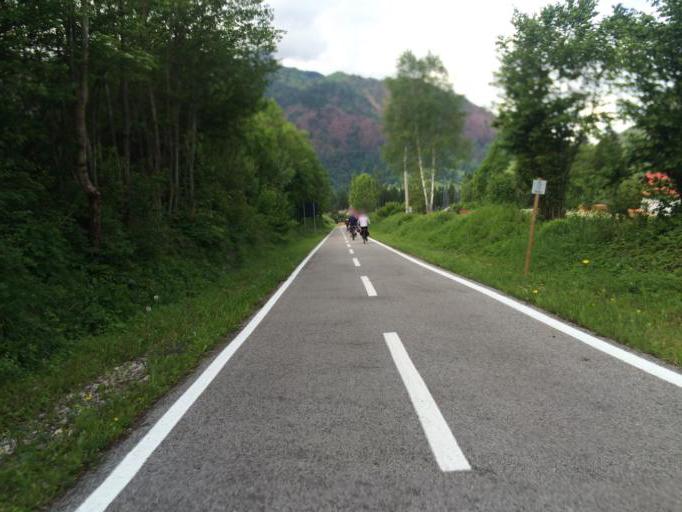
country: IT
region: Friuli Venezia Giulia
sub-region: Provincia di Udine
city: Malborghetto
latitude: 46.5020
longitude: 13.5041
